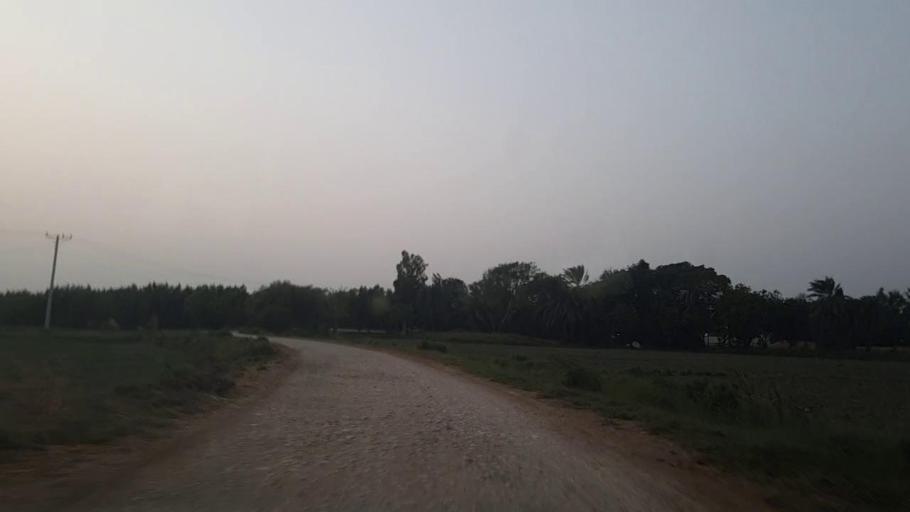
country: PK
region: Sindh
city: Mirpur Sakro
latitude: 24.5894
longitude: 67.7825
